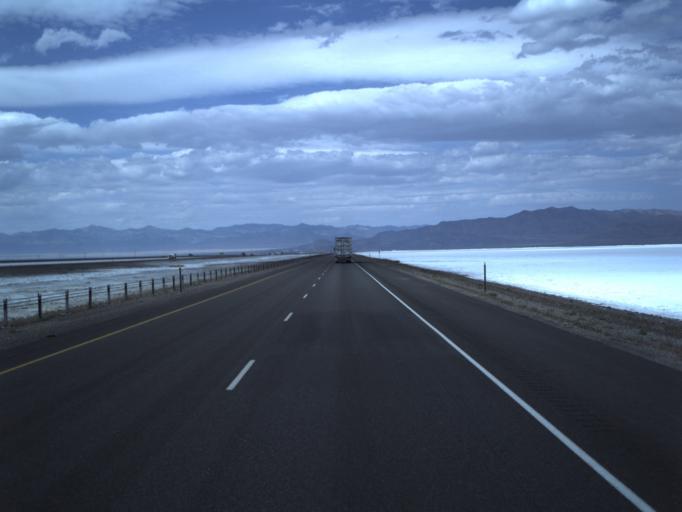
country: US
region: Utah
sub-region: Tooele County
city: Wendover
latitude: 40.7398
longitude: -113.8720
